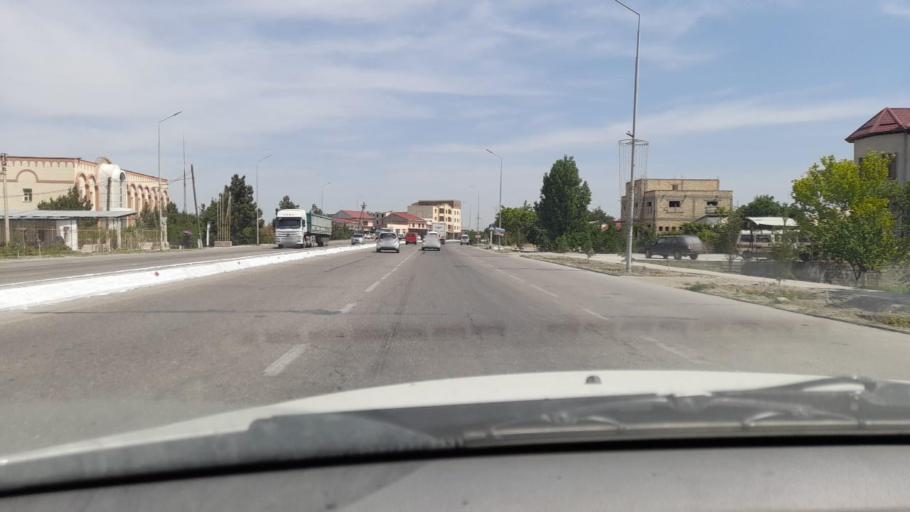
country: UZ
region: Bukhara
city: Galaosiyo
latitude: 39.8608
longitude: 64.4439
